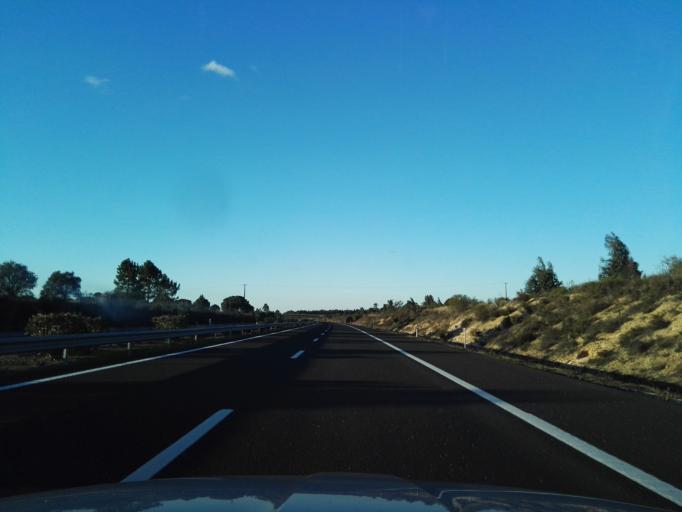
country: PT
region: Santarem
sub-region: Benavente
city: Poceirao
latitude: 38.7812
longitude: -8.6849
